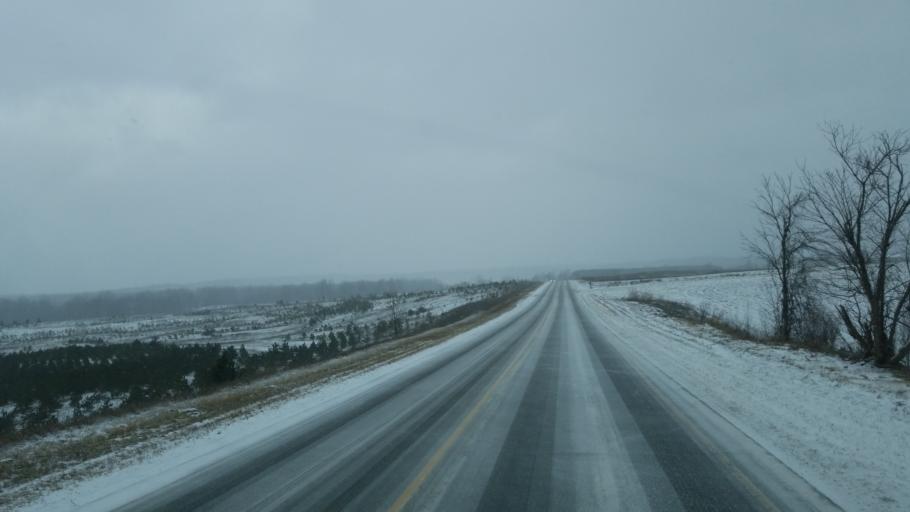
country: US
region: Michigan
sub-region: Osceola County
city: Reed City
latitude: 43.8448
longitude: -85.4239
